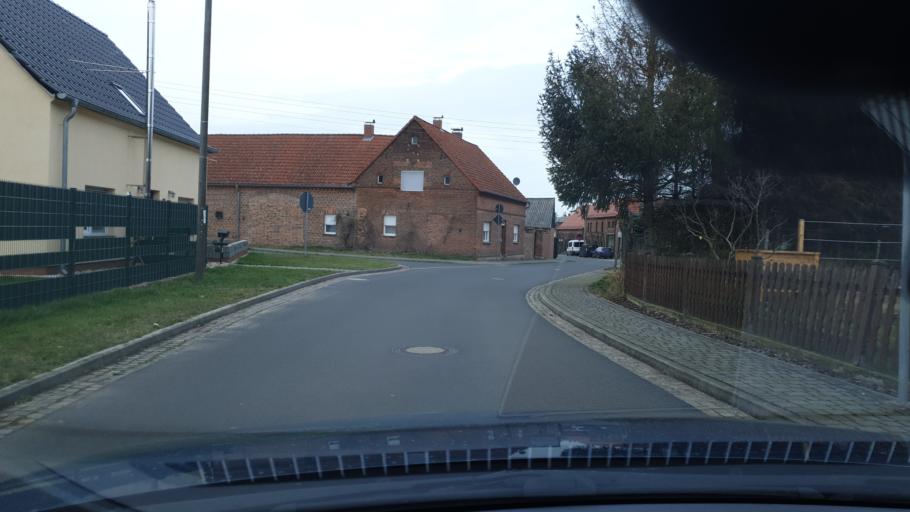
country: DE
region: Saxony-Anhalt
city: Radis
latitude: 51.7623
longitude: 12.5566
